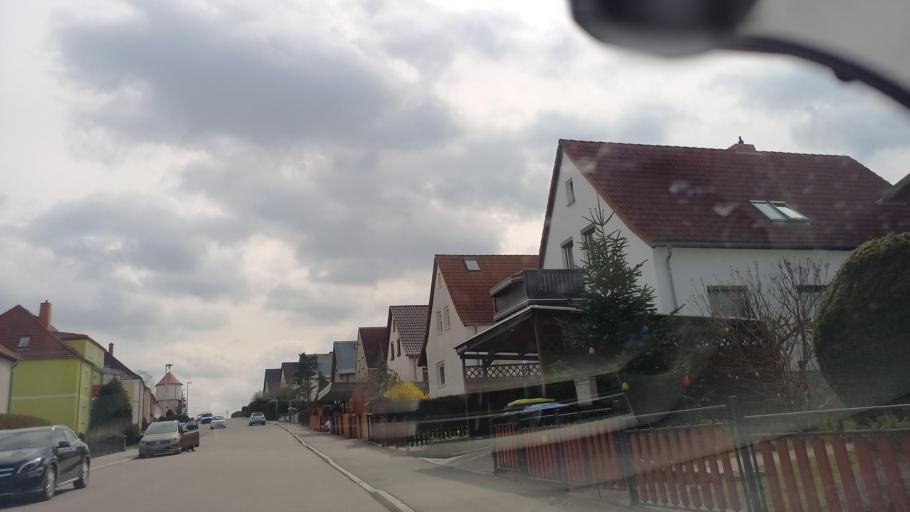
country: DE
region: Saxony
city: Wilkau-Hasslau
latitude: 50.6984
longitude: 12.5179
